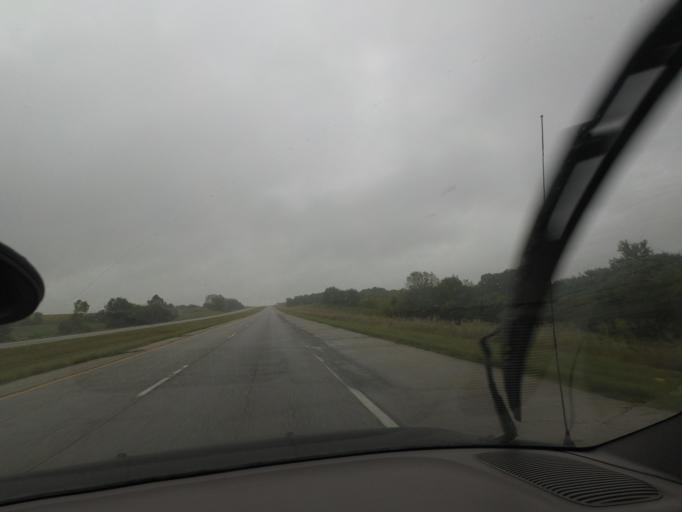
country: US
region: Illinois
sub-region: Pike County
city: Barry
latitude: 39.6924
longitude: -90.9849
